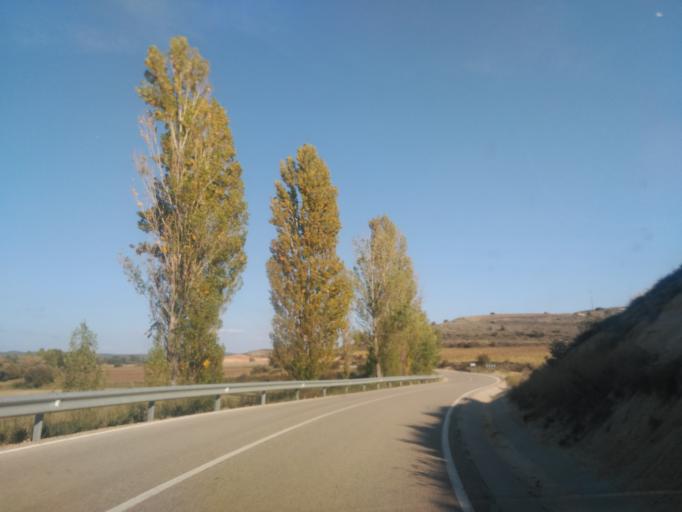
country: ES
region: Castille and Leon
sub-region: Provincia de Soria
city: Alcubilla de Avellaneda
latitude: 41.7553
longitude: -3.2625
